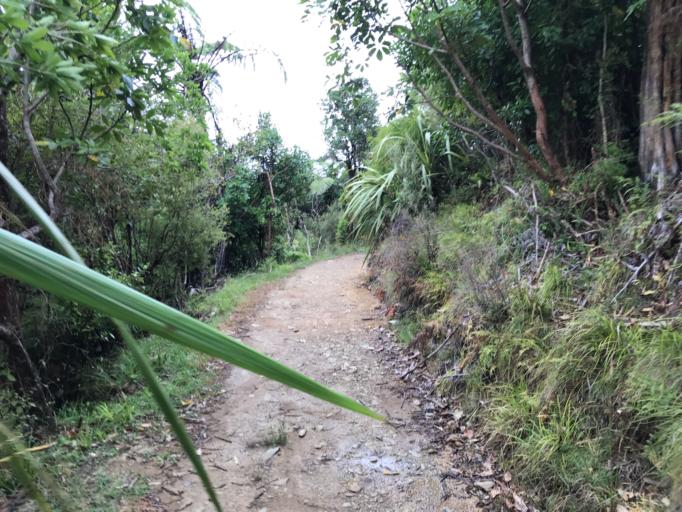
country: NZ
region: Marlborough
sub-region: Marlborough District
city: Picton
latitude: -41.1073
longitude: 174.1448
